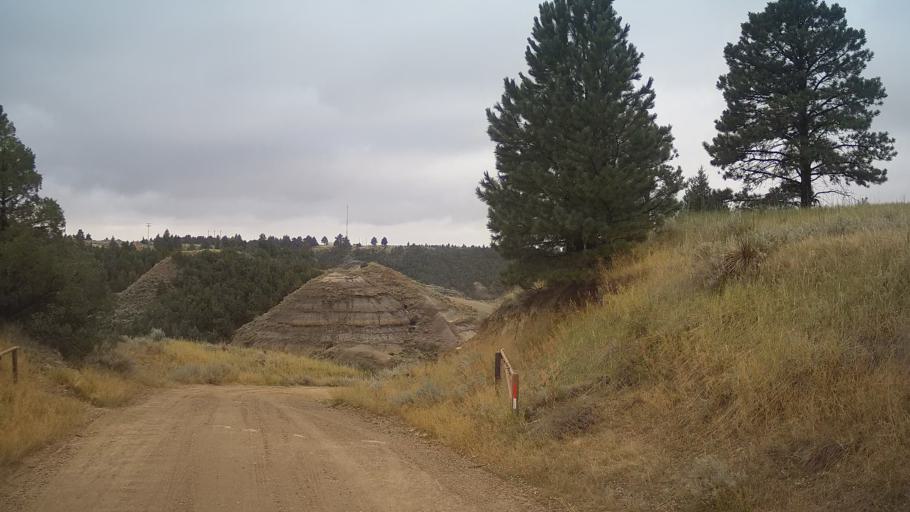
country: US
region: Montana
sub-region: Dawson County
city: Glendive
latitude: 47.0511
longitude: -104.6777
